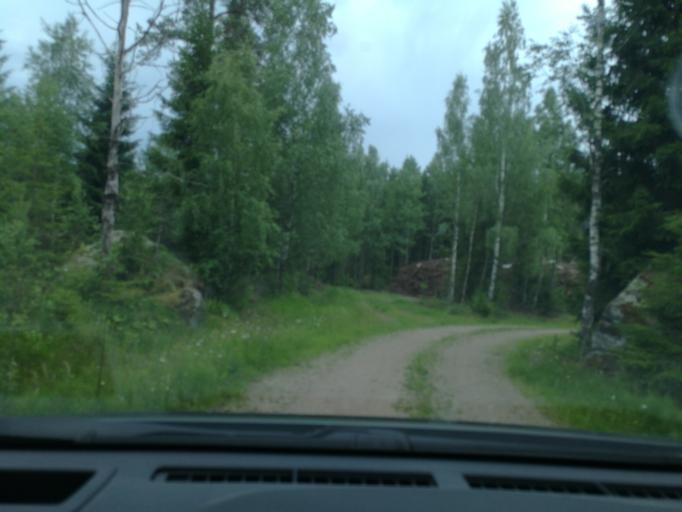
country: SE
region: Vaestmanland
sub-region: Surahammars Kommun
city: Ramnas
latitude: 59.8103
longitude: 16.3220
